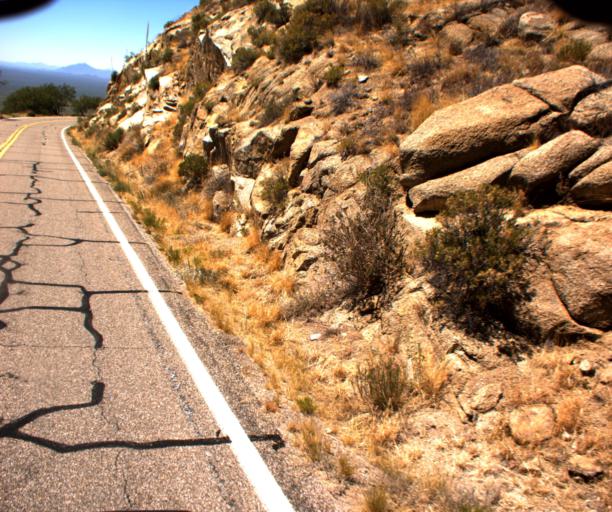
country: US
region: Arizona
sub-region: Pima County
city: Sells
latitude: 31.9771
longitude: -111.6037
